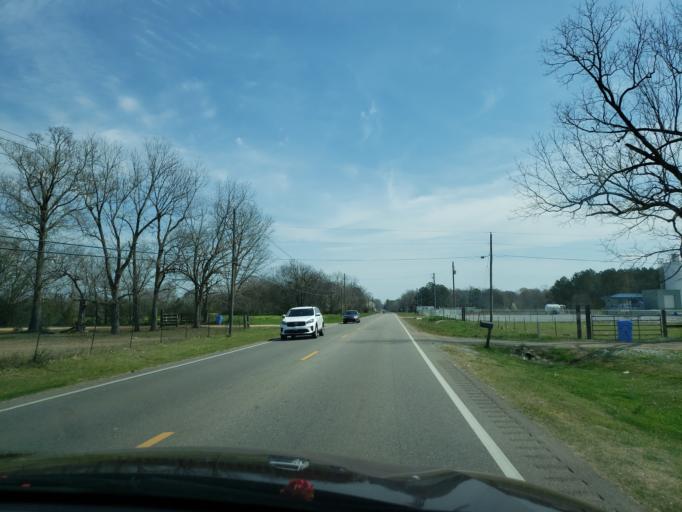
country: US
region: Alabama
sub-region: Autauga County
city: Prattville
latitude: 32.4307
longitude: -86.5117
